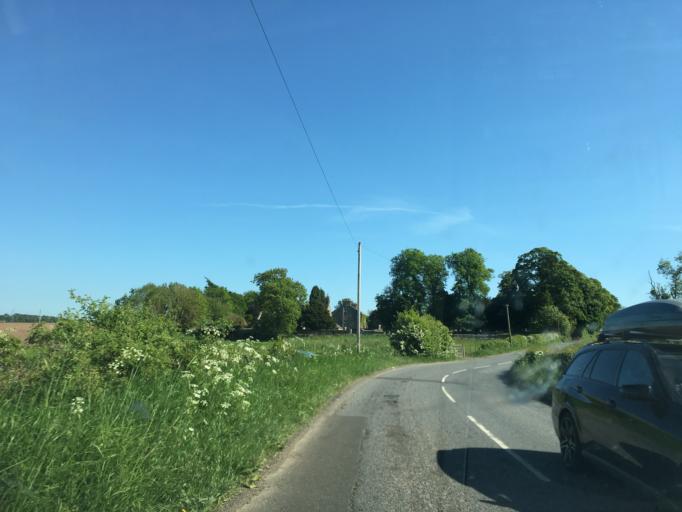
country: GB
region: Scotland
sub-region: Perth and Kinross
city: Methven
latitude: 56.3945
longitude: -3.5391
